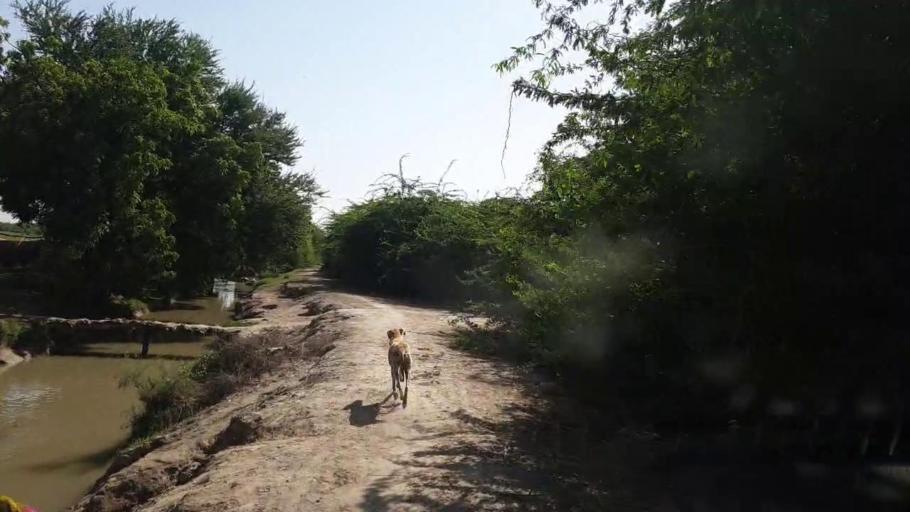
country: PK
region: Sindh
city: Kadhan
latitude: 24.6284
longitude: 68.9938
